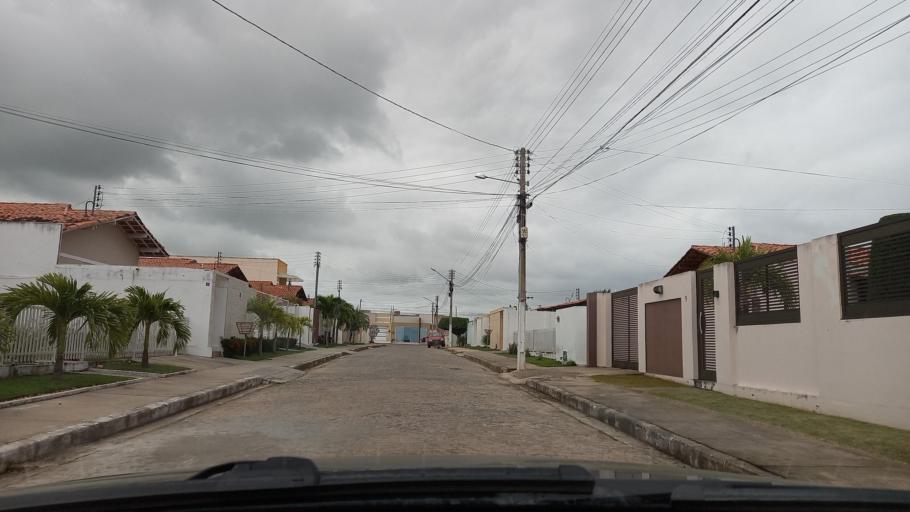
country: BR
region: Sergipe
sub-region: Caninde De Sao Francisco
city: Caninde de Sao Francisco
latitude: -9.6133
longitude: -37.7643
